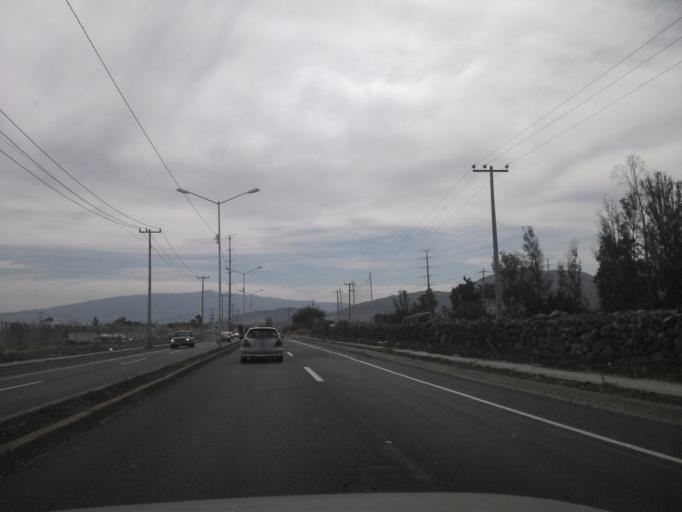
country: MX
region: Jalisco
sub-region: Tlajomulco de Zuniga
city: Villas de la Hacienda [Fraccionamiento]
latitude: 20.5435
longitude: -103.4025
